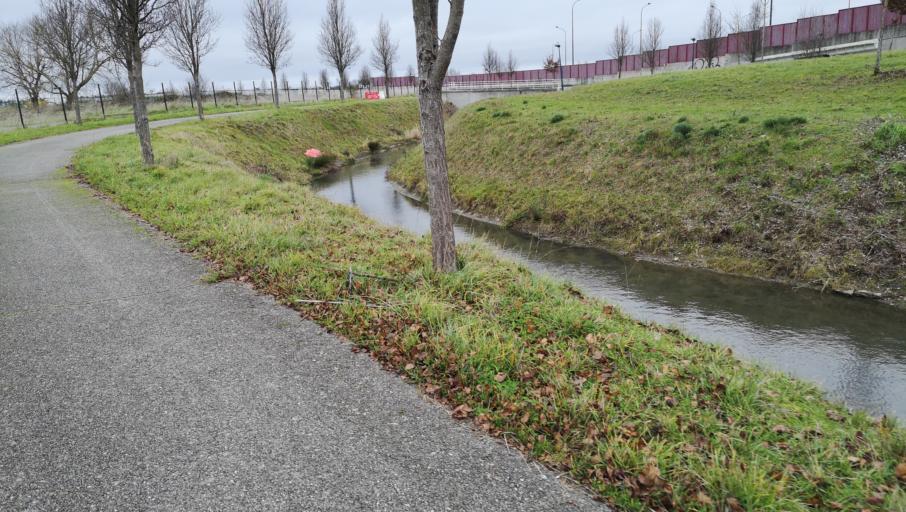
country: FR
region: Midi-Pyrenees
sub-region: Departement de la Haute-Garonne
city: Beauzelle
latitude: 43.6640
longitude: 1.3581
